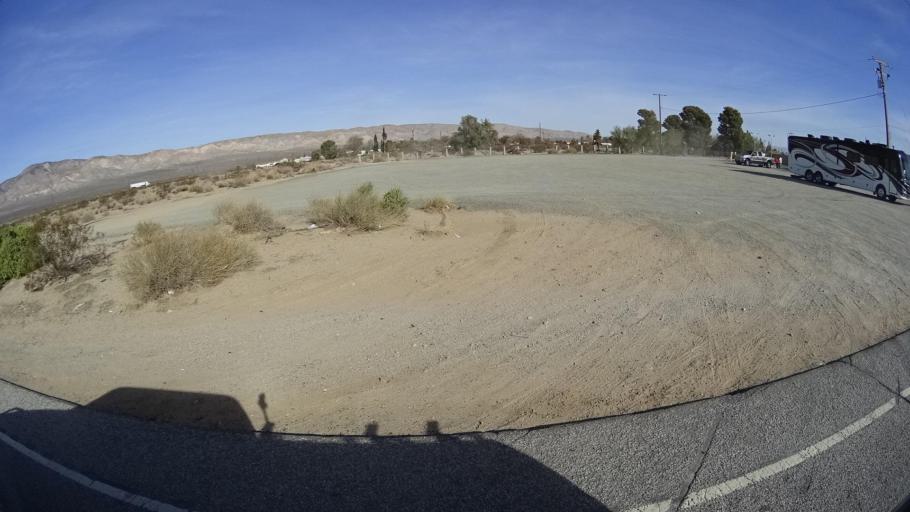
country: US
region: California
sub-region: Kern County
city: Mojave
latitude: 35.1252
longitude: -118.1182
